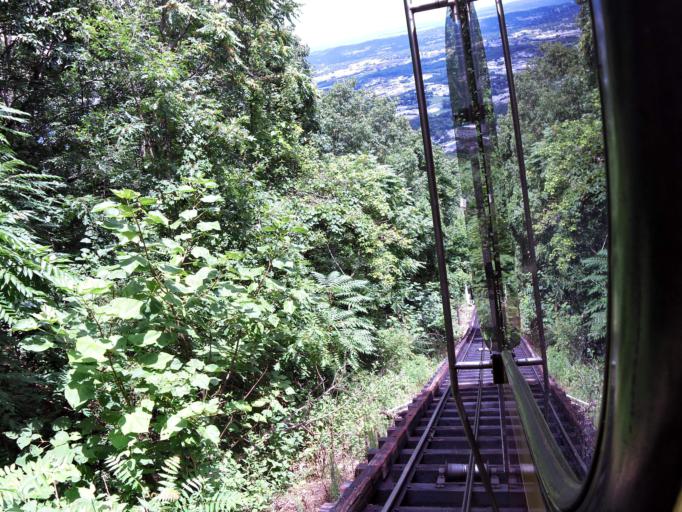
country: US
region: Tennessee
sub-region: Hamilton County
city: Lookout Mountain
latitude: 35.0064
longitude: -85.3420
